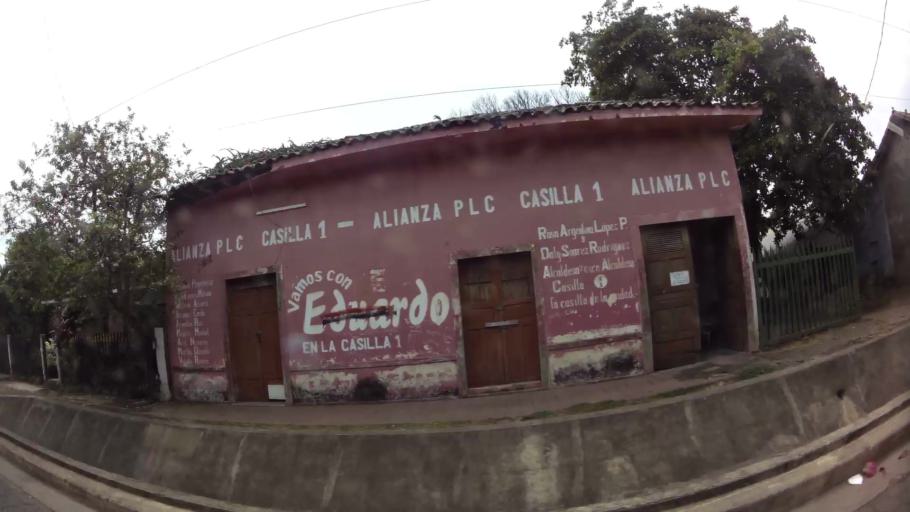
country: NI
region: Rivas
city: Rivas
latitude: 11.4418
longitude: -85.8274
